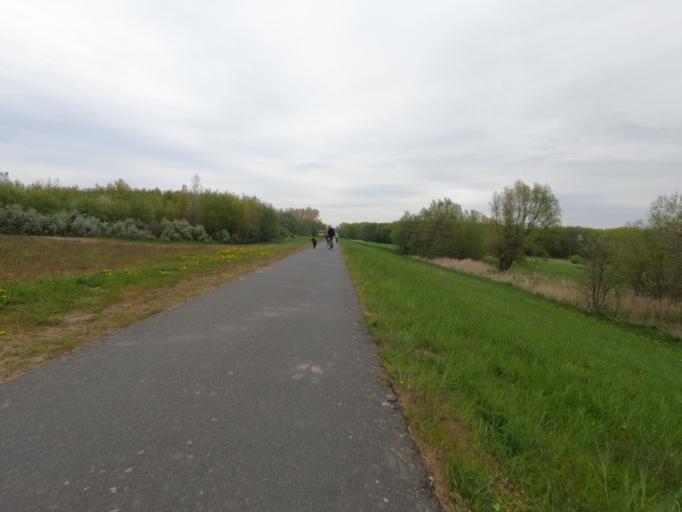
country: DE
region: Mecklenburg-Vorpommern
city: Ostseebad Dierhagen
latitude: 54.3470
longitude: 12.3859
